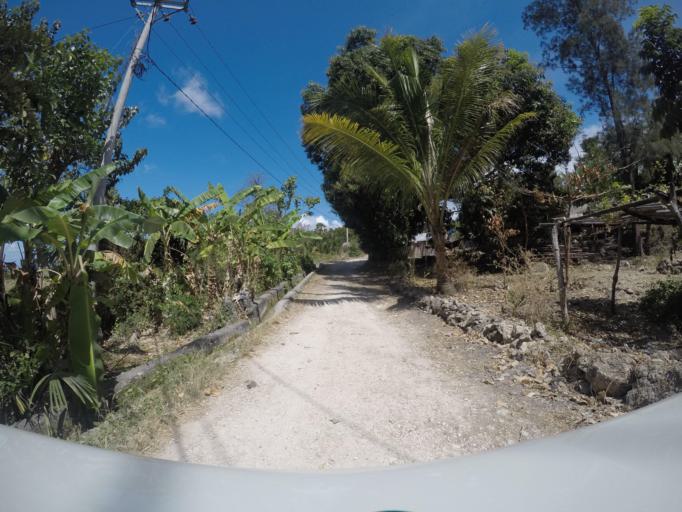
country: TL
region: Baucau
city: Baucau
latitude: -8.4503
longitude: 126.4403
